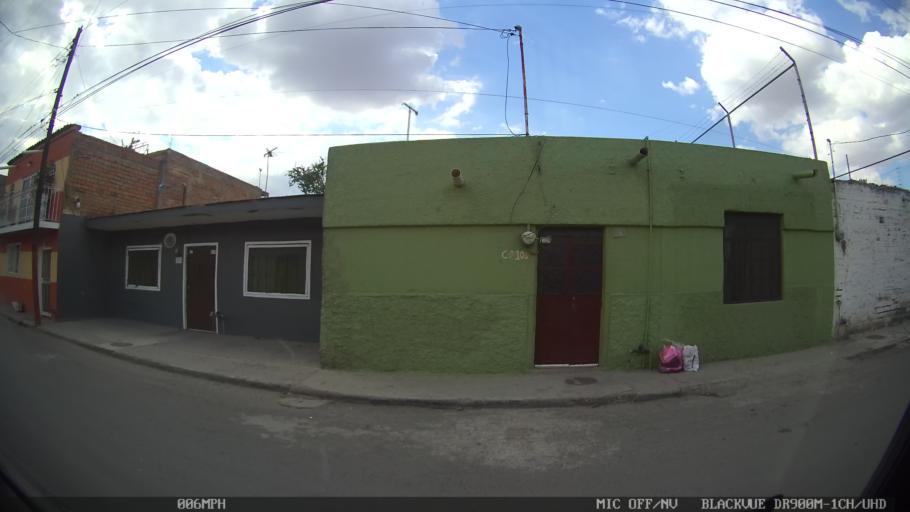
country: MX
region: Jalisco
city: Tonala
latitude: 20.6560
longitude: -103.2566
